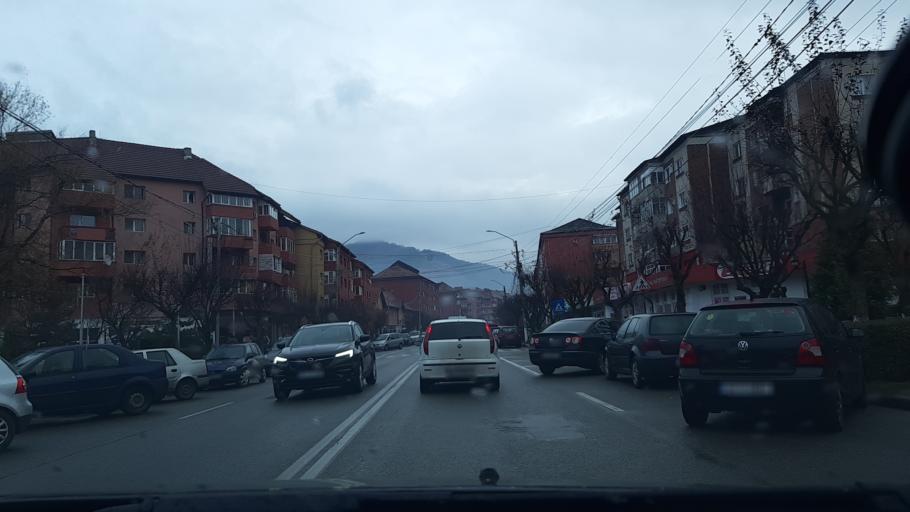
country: RO
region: Hunedoara
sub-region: Municipiul Petrosani
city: Petrosani
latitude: 45.4447
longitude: 23.3796
